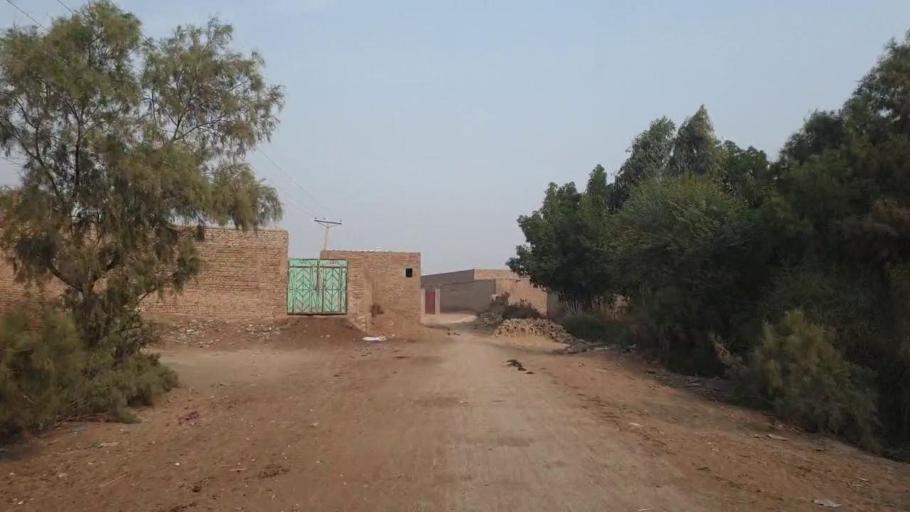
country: PK
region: Sindh
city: Sann
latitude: 26.1082
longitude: 68.0837
